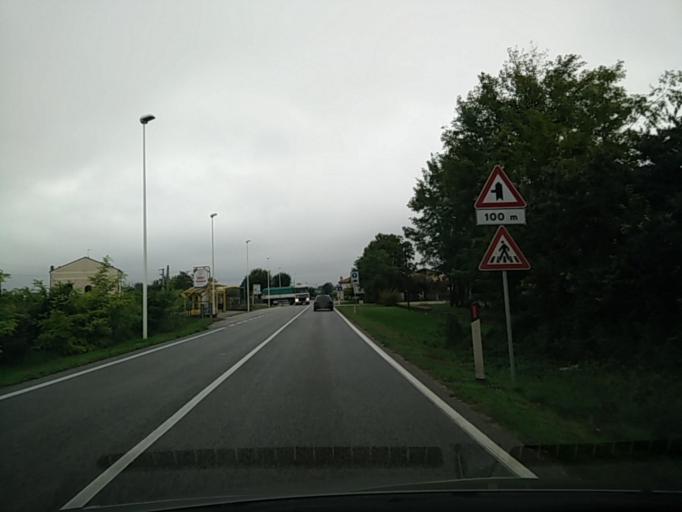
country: IT
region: Veneto
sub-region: Provincia di Treviso
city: Fossalunga
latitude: 45.6870
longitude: 12.0405
